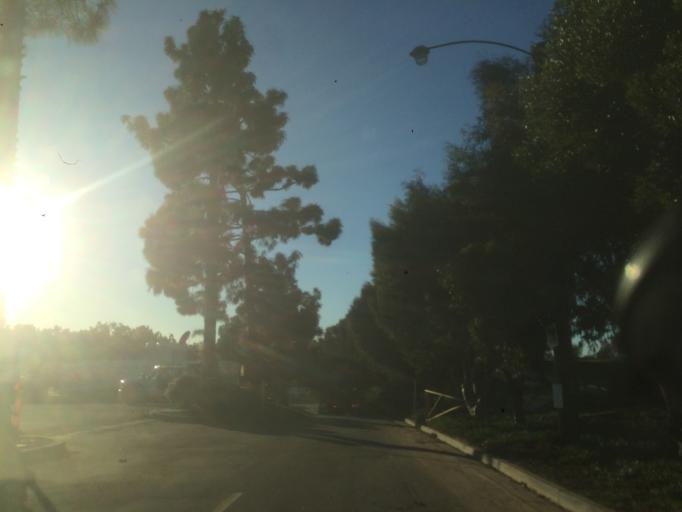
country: US
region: California
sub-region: Santa Barbara County
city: Mission Canyon
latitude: 34.4313
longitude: -119.7357
